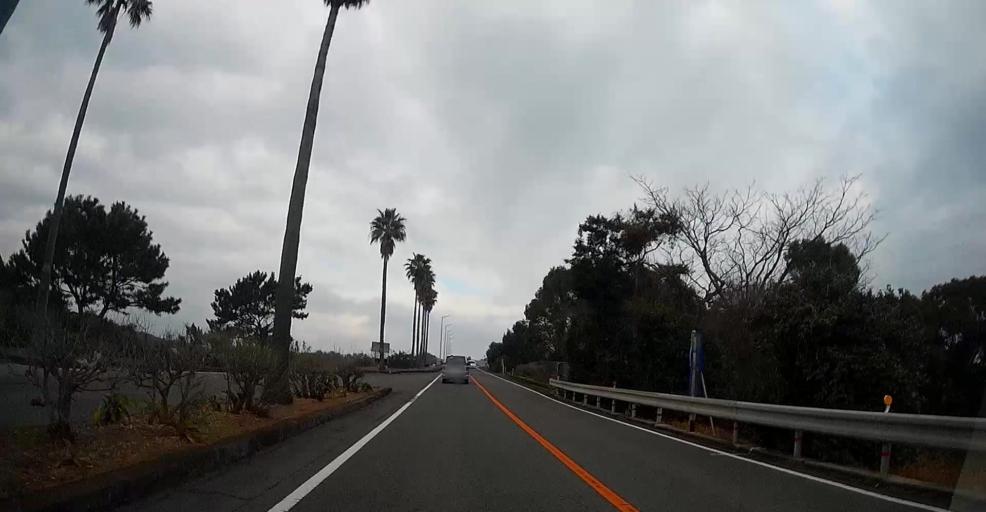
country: JP
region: Kumamoto
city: Yatsushiro
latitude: 32.5352
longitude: 130.4226
